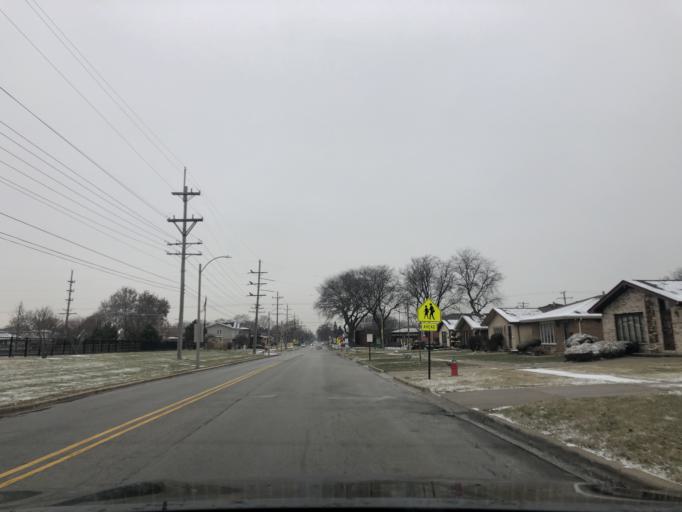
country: US
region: Illinois
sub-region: Cook County
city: Evergreen Park
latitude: 41.7282
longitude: -87.6908
